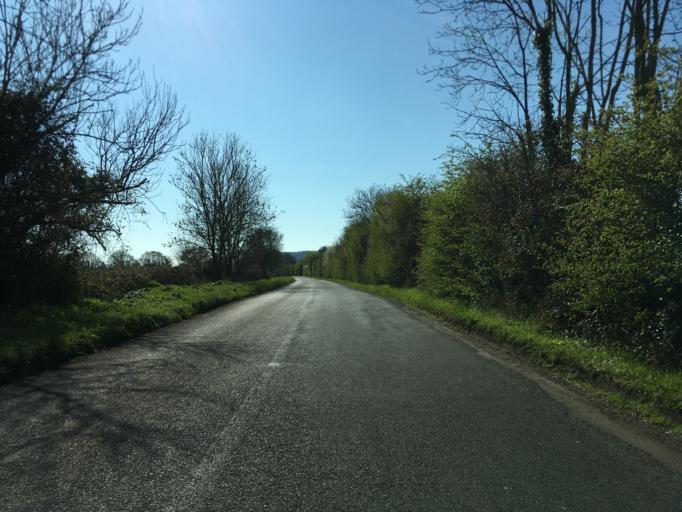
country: GB
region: England
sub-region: North Somerset
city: Portishead
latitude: 51.4800
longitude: -2.7462
